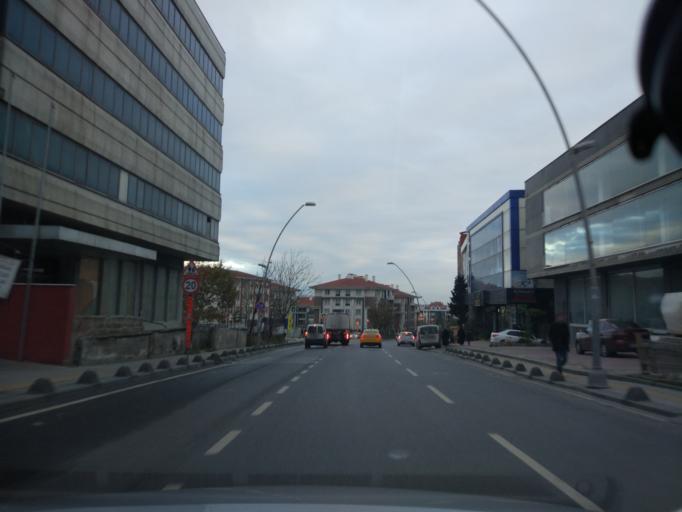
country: TR
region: Istanbul
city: Bahcelievler
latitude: 41.0140
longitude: 28.8269
